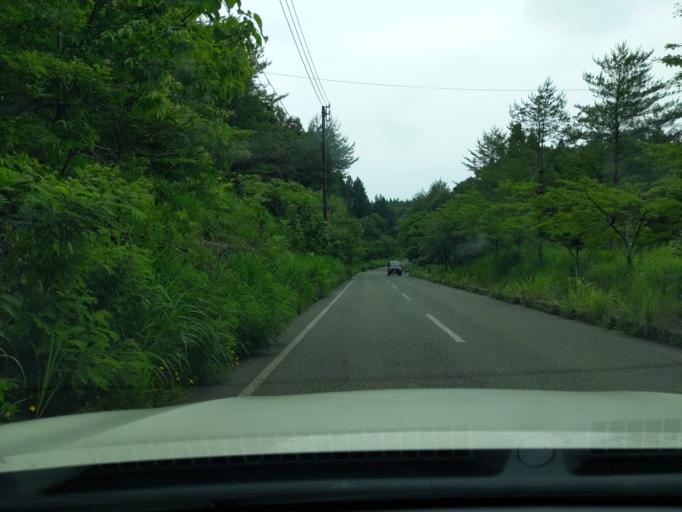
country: JP
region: Niigata
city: Kashiwazaki
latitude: 37.3363
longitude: 138.5836
